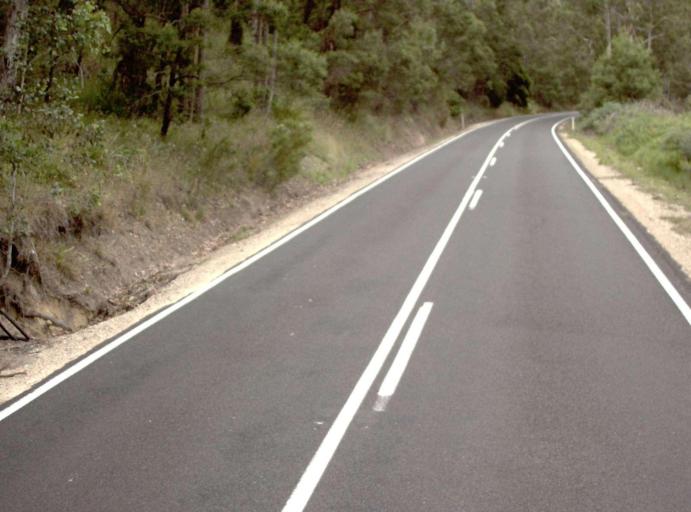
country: AU
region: New South Wales
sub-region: Bombala
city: Bombala
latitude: -37.4489
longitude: 149.1936
